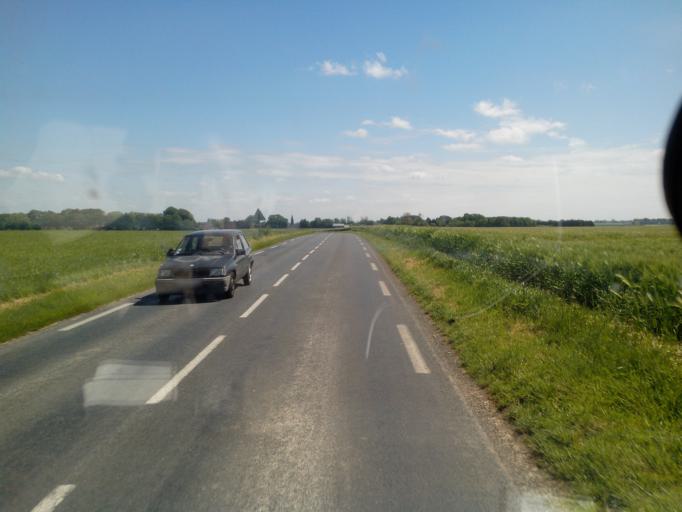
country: FR
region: Haute-Normandie
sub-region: Departement de la Seine-Maritime
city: Turretot
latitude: 49.6283
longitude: 0.2716
